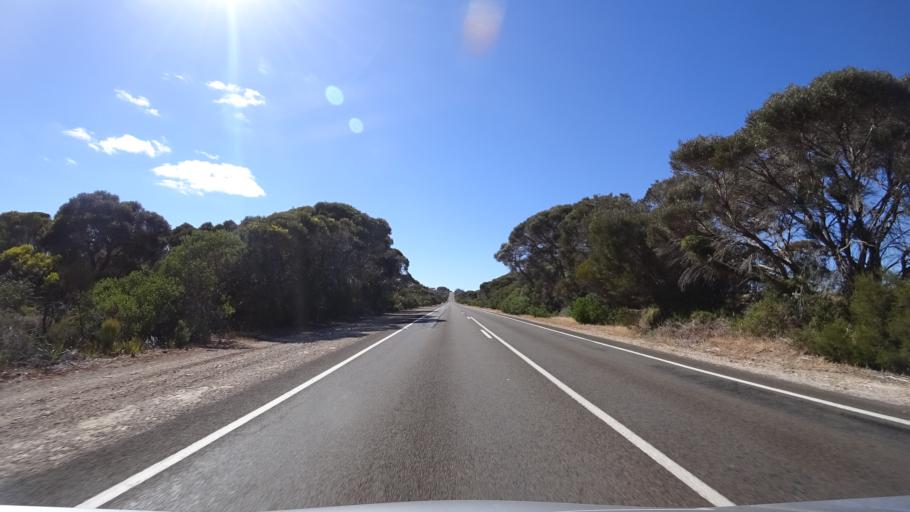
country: AU
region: South Australia
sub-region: Kangaroo Island
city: Kingscote
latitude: -35.7577
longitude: 137.6046
